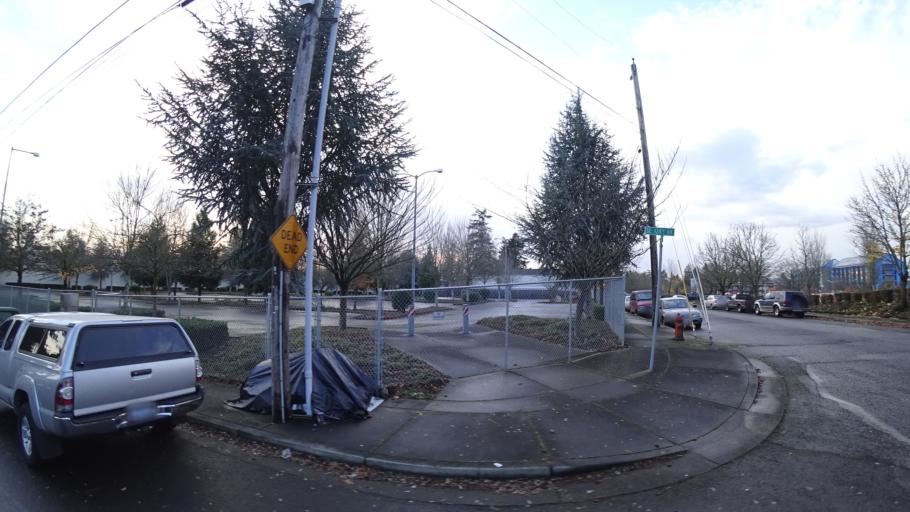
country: US
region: Oregon
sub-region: Multnomah County
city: Lents
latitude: 45.5211
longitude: -122.5352
